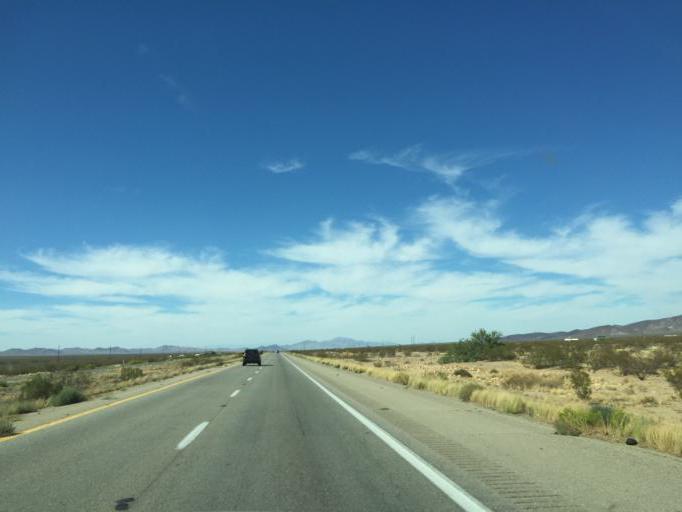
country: US
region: Arizona
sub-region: Mohave County
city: Dolan Springs
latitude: 35.5850
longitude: -114.3905
